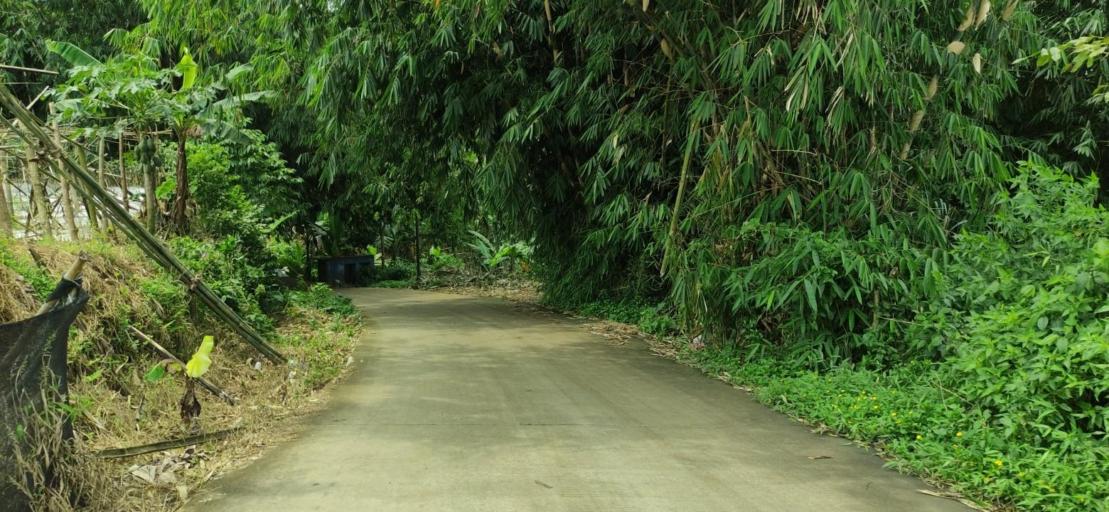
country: ID
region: West Java
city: Caringin
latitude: -6.6421
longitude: 106.8922
